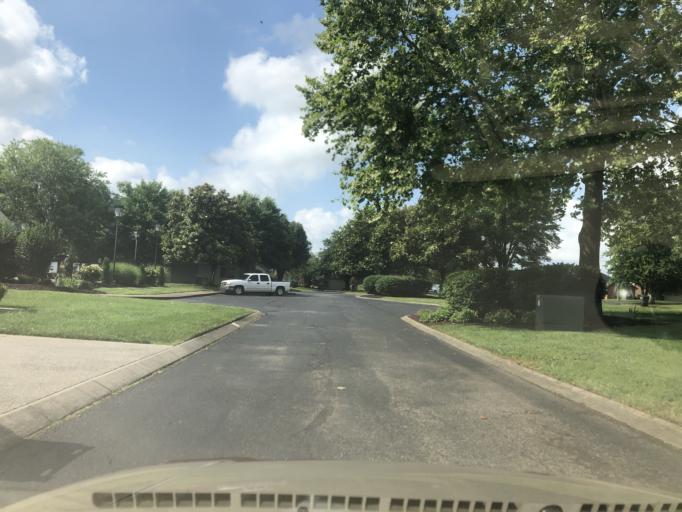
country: US
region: Tennessee
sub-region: Davidson County
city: Lakewood
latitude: 36.2254
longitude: -86.6005
